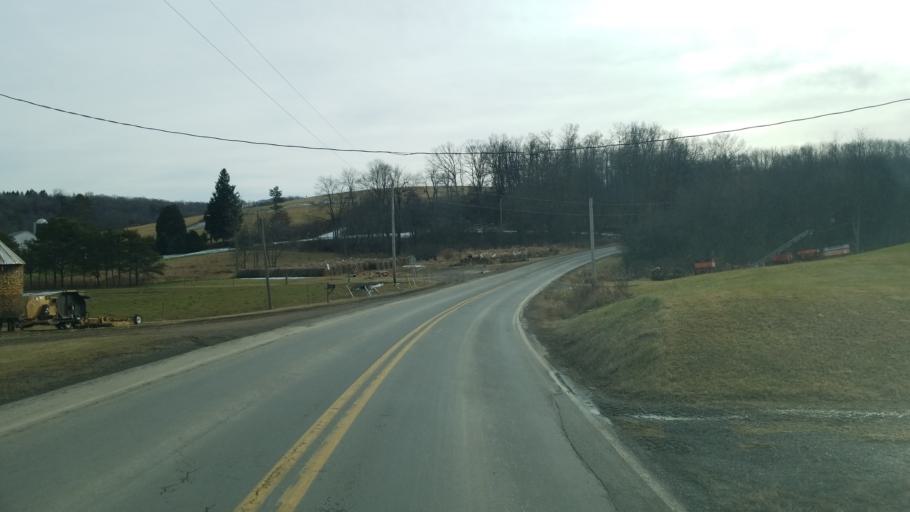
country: US
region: Pennsylvania
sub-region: Jefferson County
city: Punxsutawney
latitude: 40.8905
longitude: -79.0411
